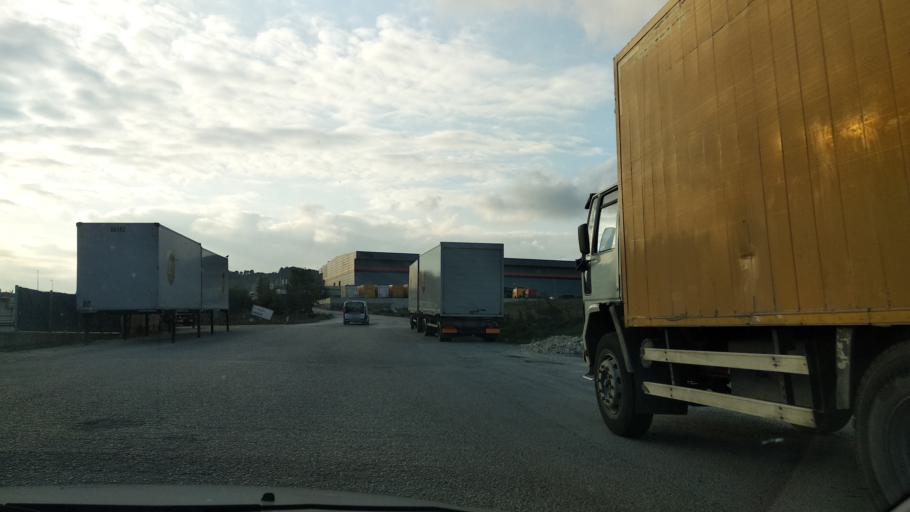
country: TR
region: Istanbul
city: Icmeler
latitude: 40.9201
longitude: 29.3465
